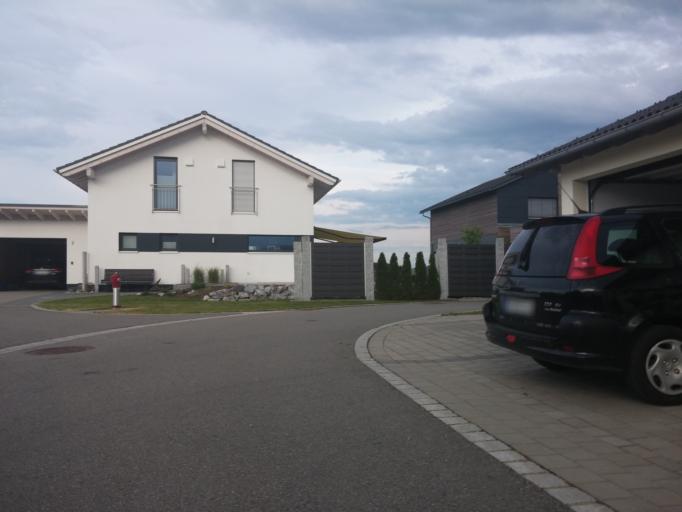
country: DE
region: Bavaria
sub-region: Swabia
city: Legau
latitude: 47.8531
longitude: 10.1298
